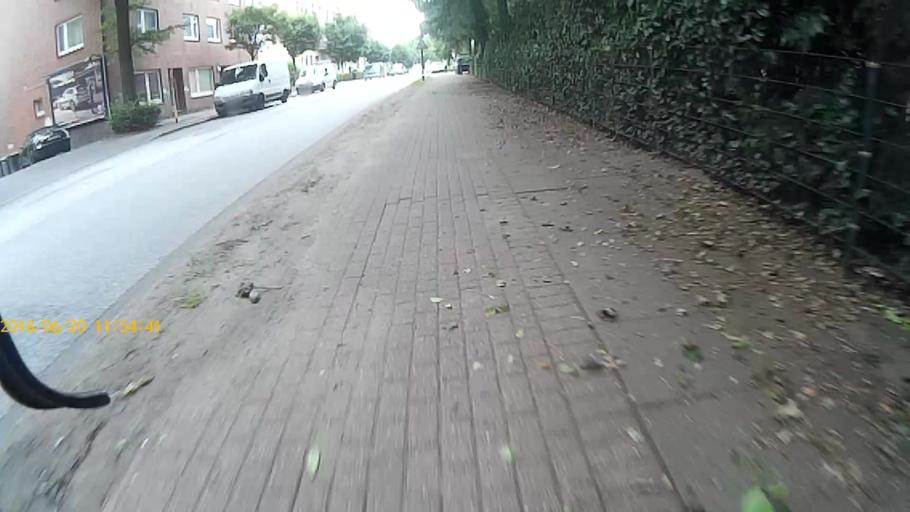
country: DE
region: Hamburg
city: Rothenburgsort
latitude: 53.5148
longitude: 10.0206
